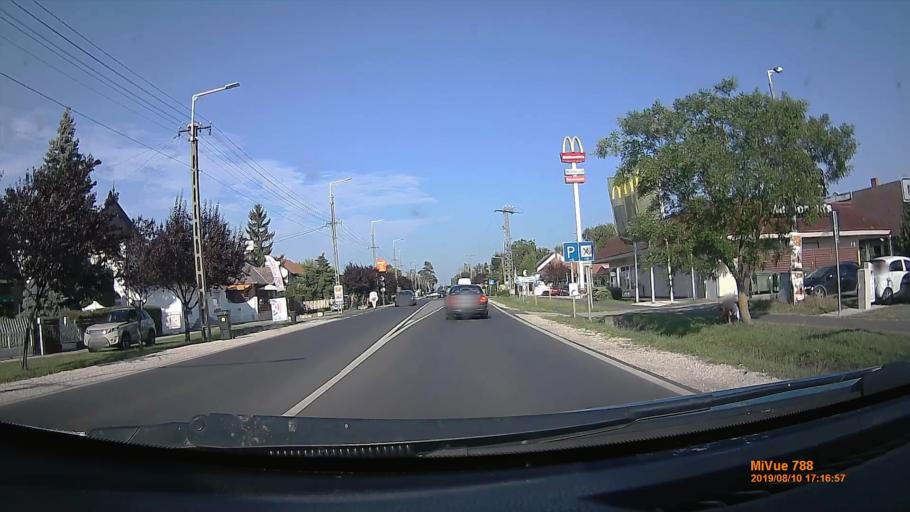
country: HU
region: Somogy
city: Balatonlelle
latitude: 46.7846
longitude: 17.6862
